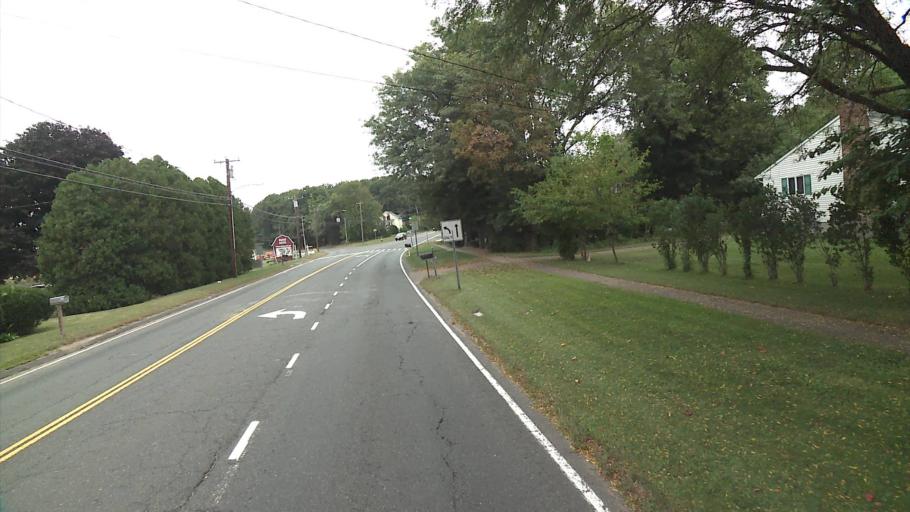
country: US
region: Connecticut
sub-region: Hartford County
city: Windsor Locks
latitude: 41.9082
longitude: -72.6791
